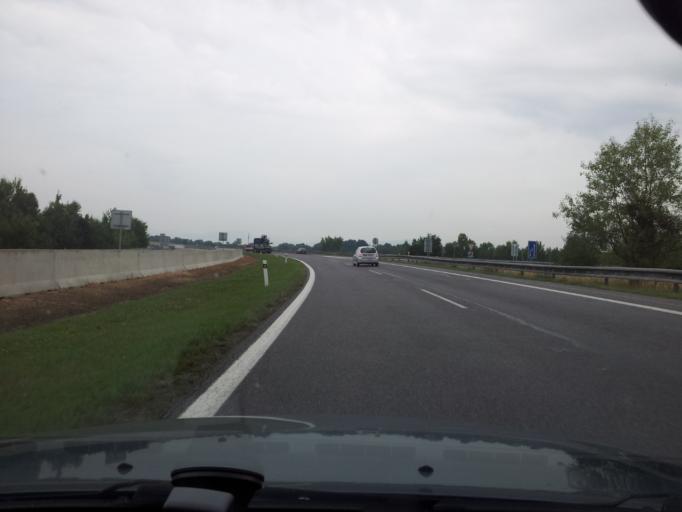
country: SK
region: Banskobystricky
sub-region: Okres Banska Bystrica
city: Zvolen
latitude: 48.6061
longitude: 19.1213
